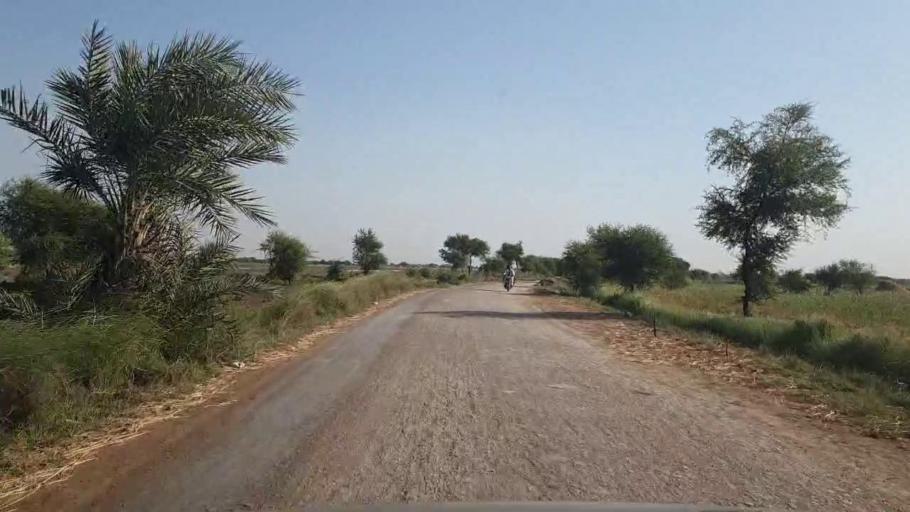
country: PK
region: Sindh
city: Matli
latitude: 25.0513
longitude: 68.7228
